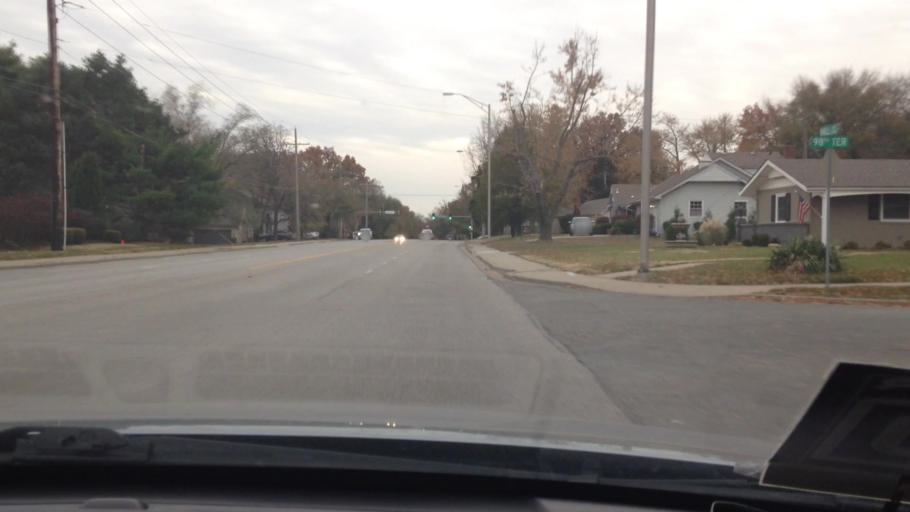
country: US
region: Kansas
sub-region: Johnson County
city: Leawood
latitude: 38.9512
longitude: -94.6491
